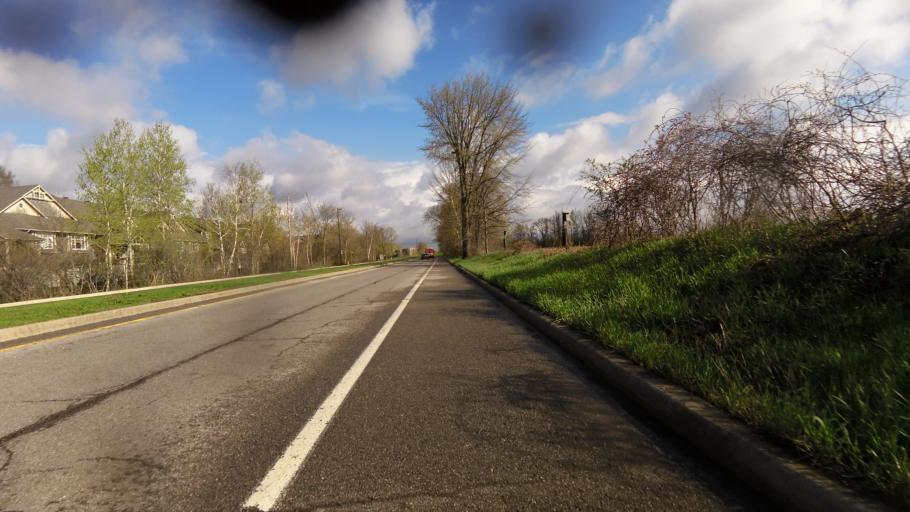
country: CA
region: Ontario
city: Bells Corners
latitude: 45.3446
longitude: -75.9005
